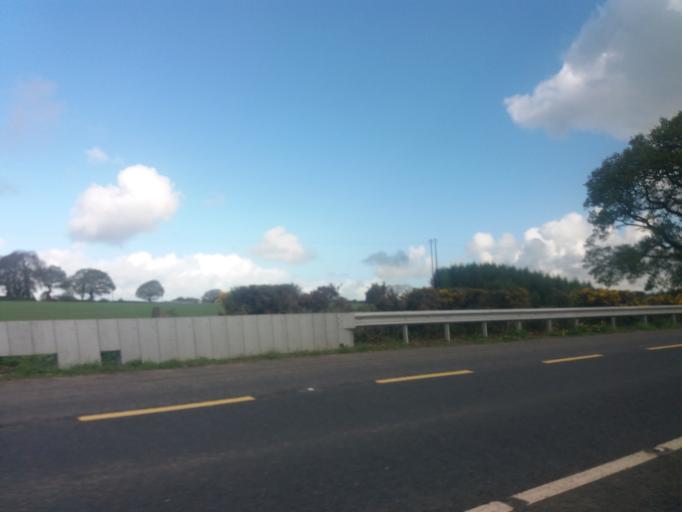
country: IE
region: Leinster
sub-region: Loch Garman
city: Ferns
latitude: 52.5789
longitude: -6.5158
